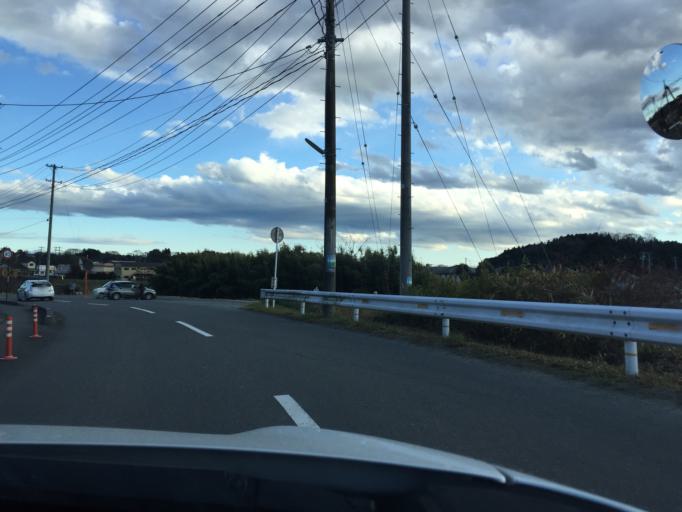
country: JP
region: Fukushima
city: Iwaki
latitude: 37.0633
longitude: 140.8676
